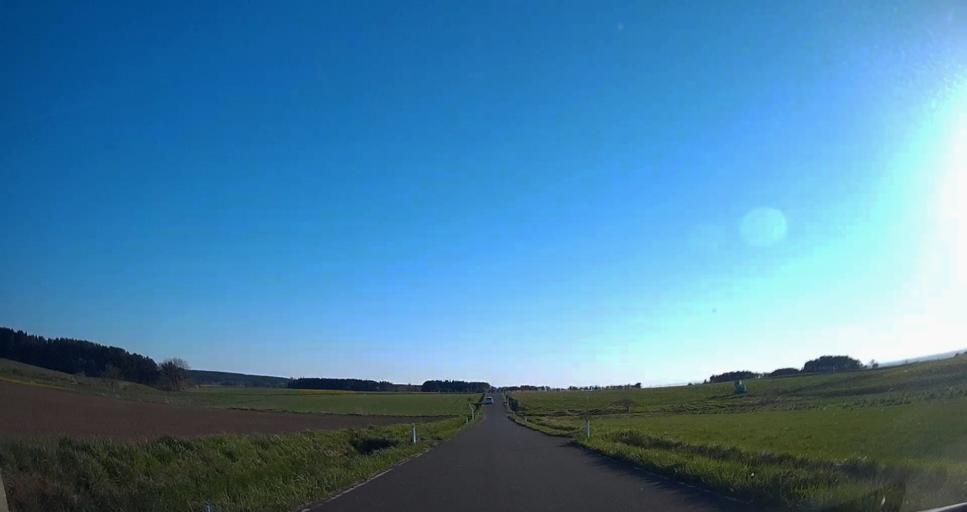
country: JP
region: Aomori
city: Mutsu
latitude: 41.1184
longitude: 141.2768
